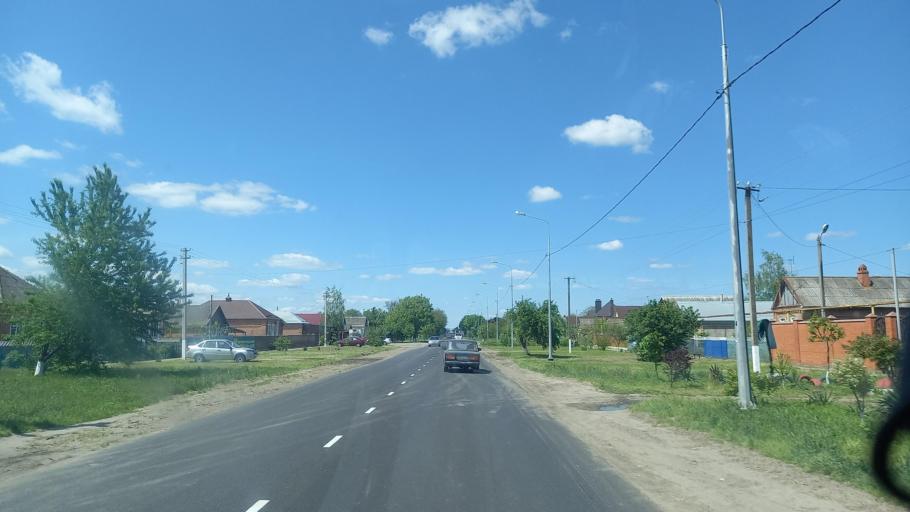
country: RU
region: Krasnodarskiy
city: Tbilisskaya
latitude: 45.3266
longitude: 40.2510
